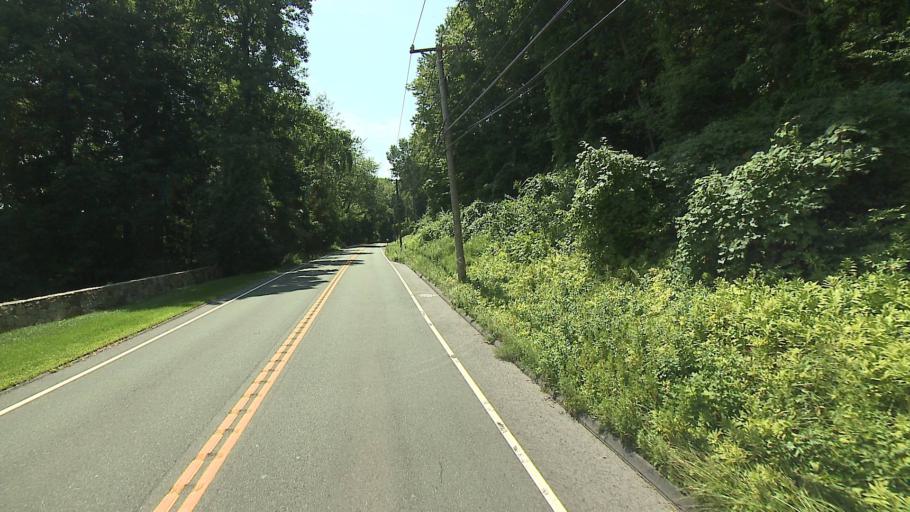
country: US
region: New York
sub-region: Putnam County
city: Putnam Lake
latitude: 41.4882
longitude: -73.4652
